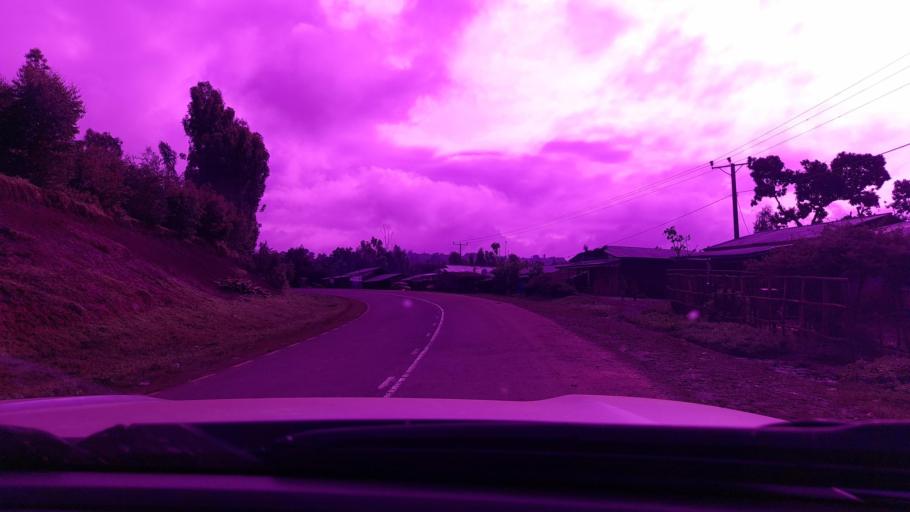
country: ET
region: Oromiya
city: Bedele
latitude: 8.2278
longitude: 36.4510
